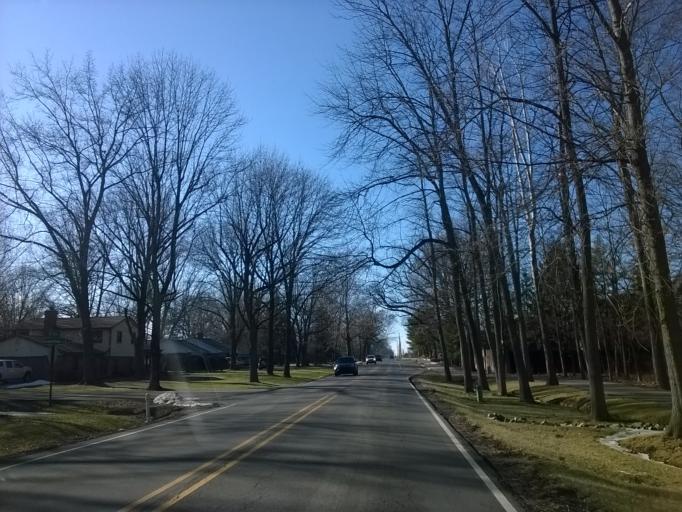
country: US
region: Indiana
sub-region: Boone County
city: Zionsville
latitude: 39.9411
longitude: -86.2133
